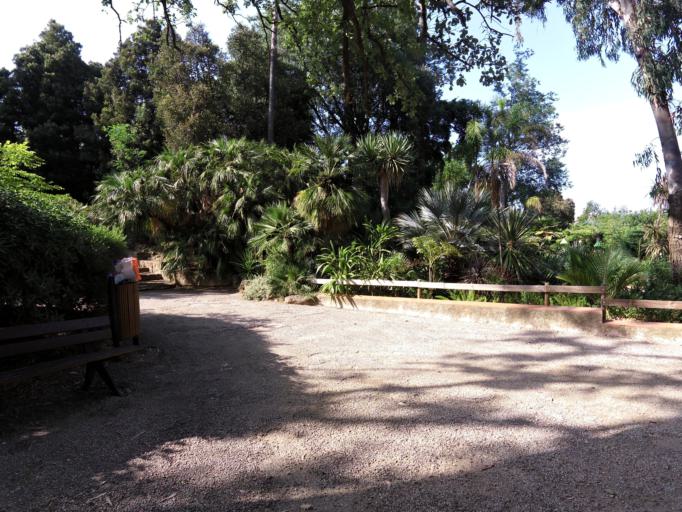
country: FR
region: Provence-Alpes-Cote d'Azur
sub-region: Departement du Var
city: Hyeres
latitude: 43.1105
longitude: 6.1356
